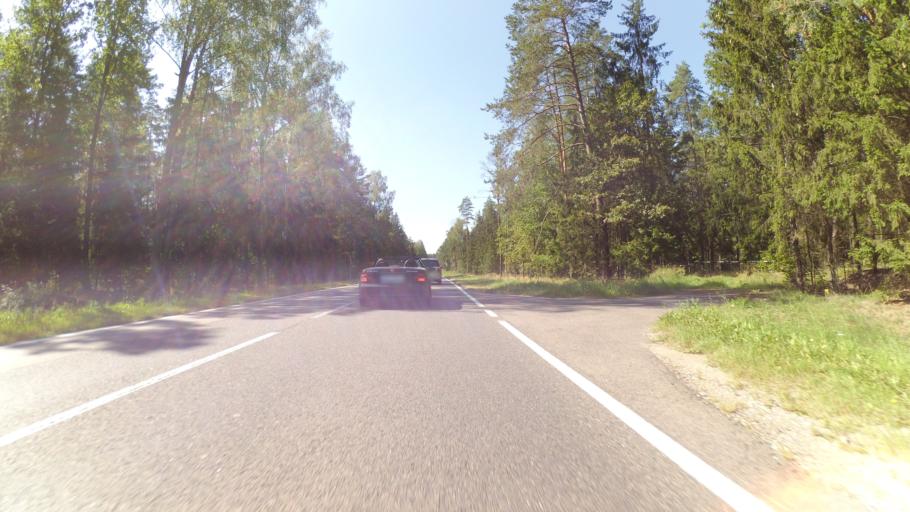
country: PL
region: Podlasie
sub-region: Powiat bialostocki
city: Suprasl
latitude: 53.1300
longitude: 23.4292
